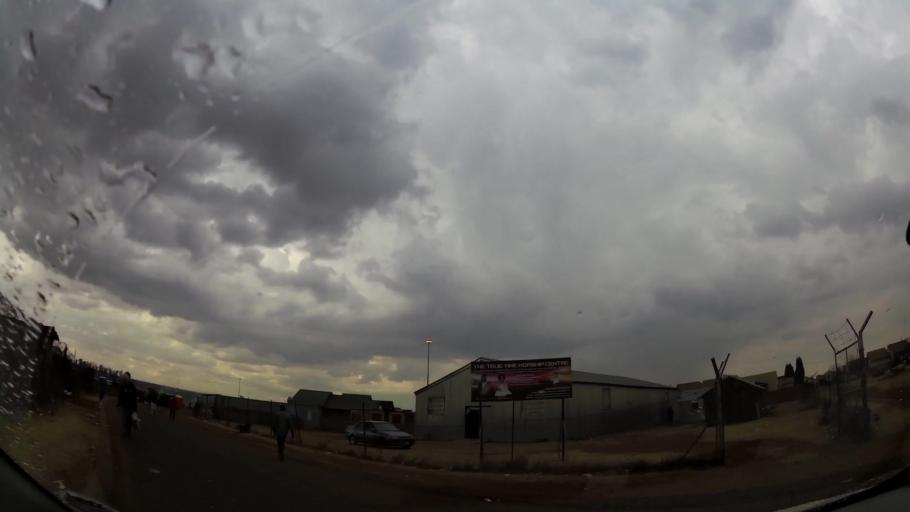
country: ZA
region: Gauteng
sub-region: Ekurhuleni Metropolitan Municipality
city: Germiston
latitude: -26.3680
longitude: 28.1643
